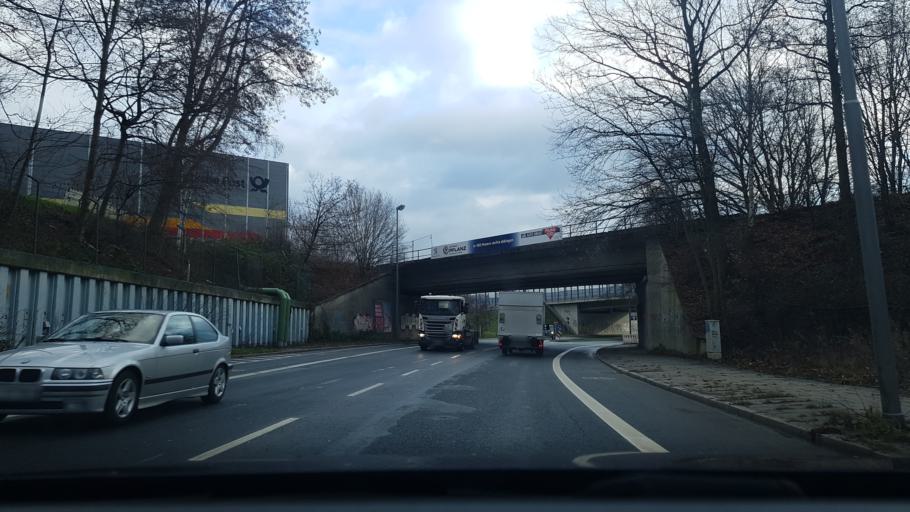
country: DE
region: North Rhine-Westphalia
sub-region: Regierungsbezirk Arnsberg
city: Bochum
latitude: 51.4635
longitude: 7.2610
